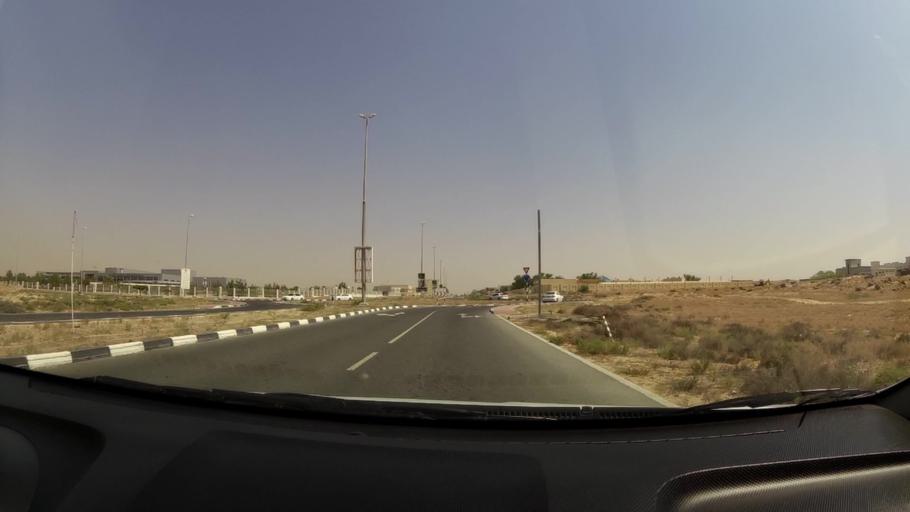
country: AE
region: Umm al Qaywayn
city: Umm al Qaywayn
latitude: 25.5032
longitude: 55.5958
